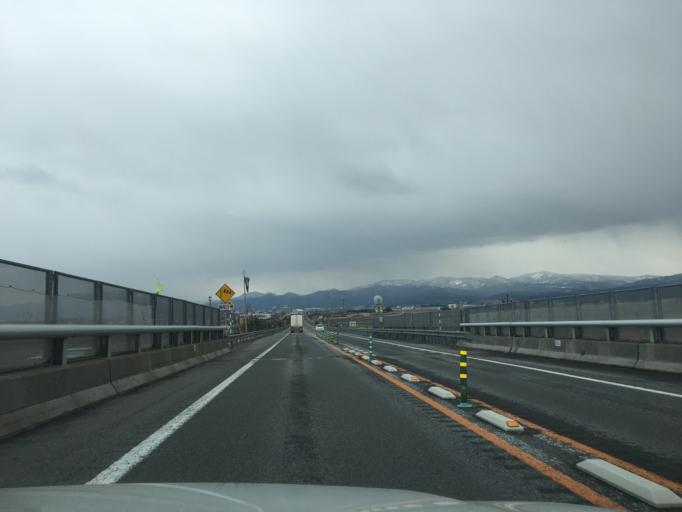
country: JP
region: Aomori
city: Aomori Shi
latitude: 40.7976
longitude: 140.7111
